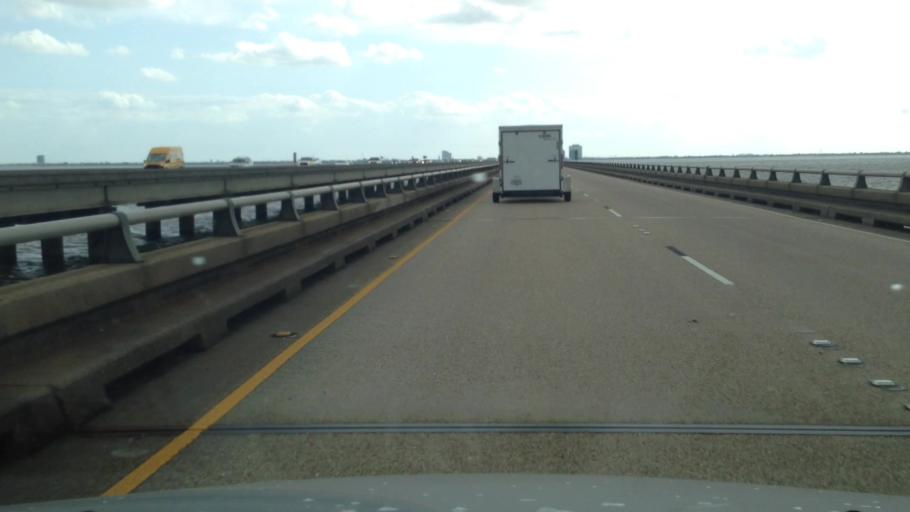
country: US
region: Louisiana
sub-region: Jefferson Parish
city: Metairie
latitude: 30.0617
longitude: -90.1471
